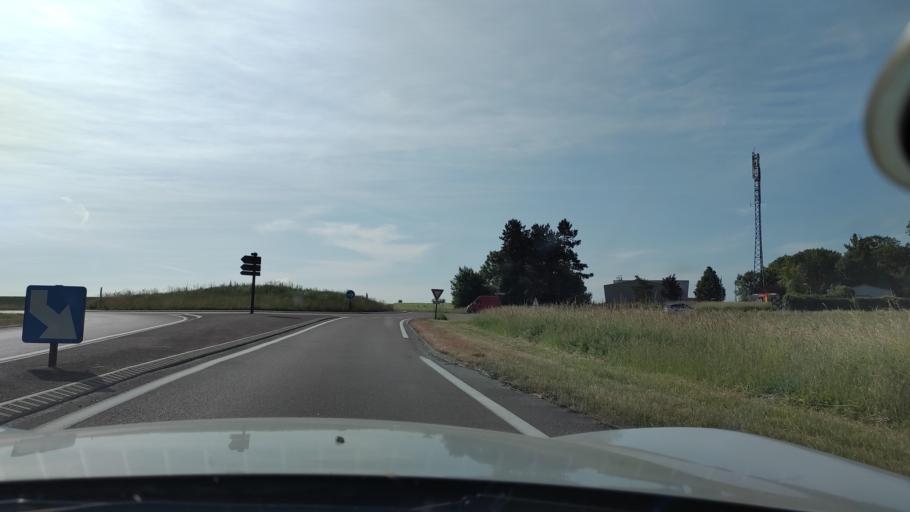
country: FR
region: Ile-de-France
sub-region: Departement de Seine-et-Marne
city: Chenoise
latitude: 48.6218
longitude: 3.1947
